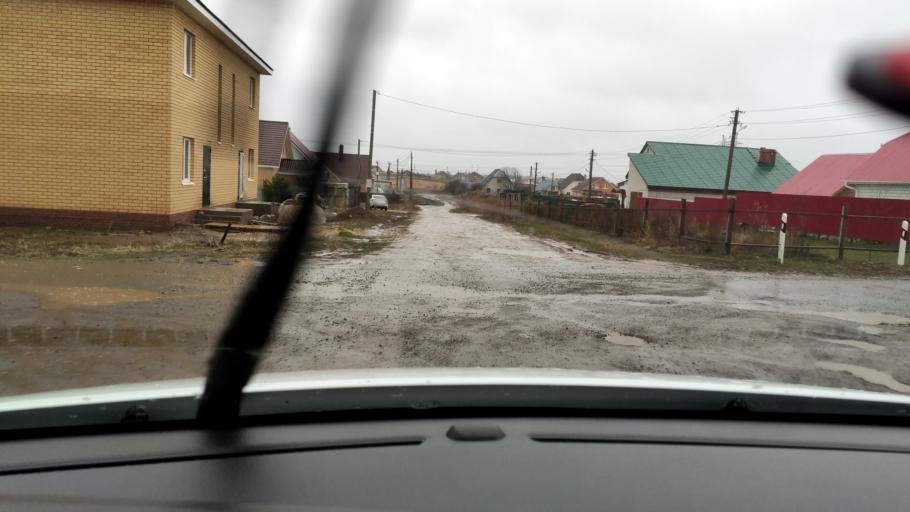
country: RU
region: Tatarstan
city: Vysokaya Gora
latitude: 55.9084
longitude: 49.3210
